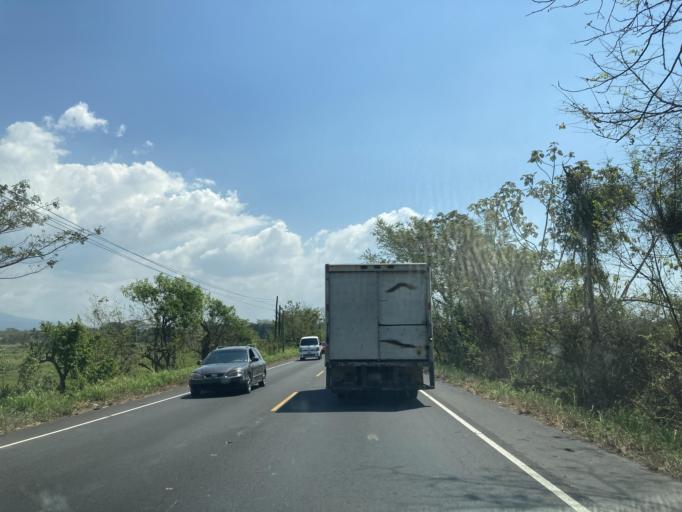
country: GT
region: Santa Rosa
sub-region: Municipio de Taxisco
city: Taxisco
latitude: 14.0949
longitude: -90.5895
